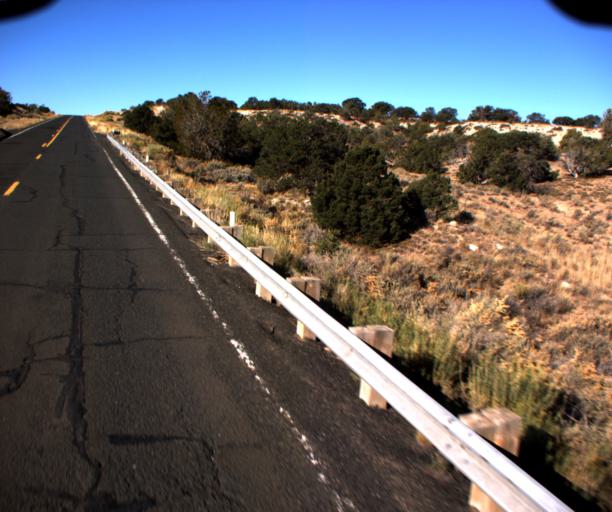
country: US
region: Arizona
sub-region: Navajo County
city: First Mesa
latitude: 35.7659
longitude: -109.9912
